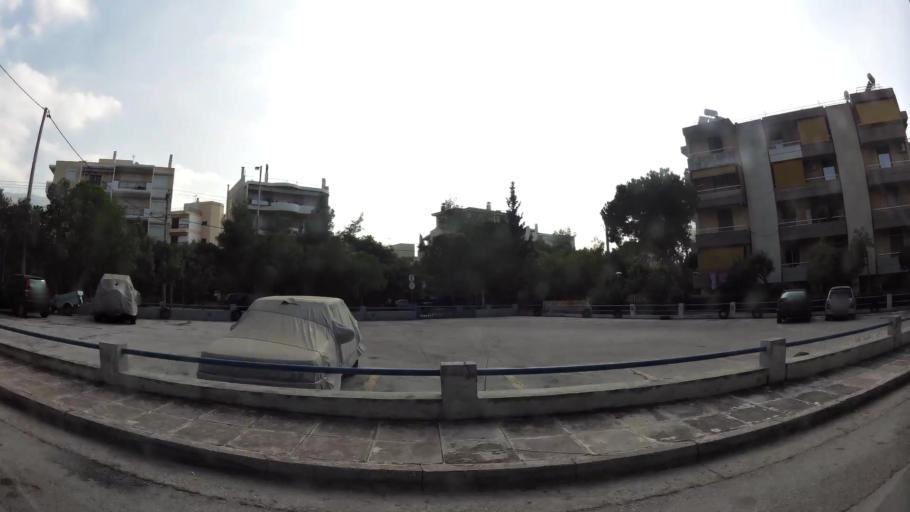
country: GR
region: Attica
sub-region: Nomarchia Athinas
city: Papagou
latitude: 37.9850
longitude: 23.7883
